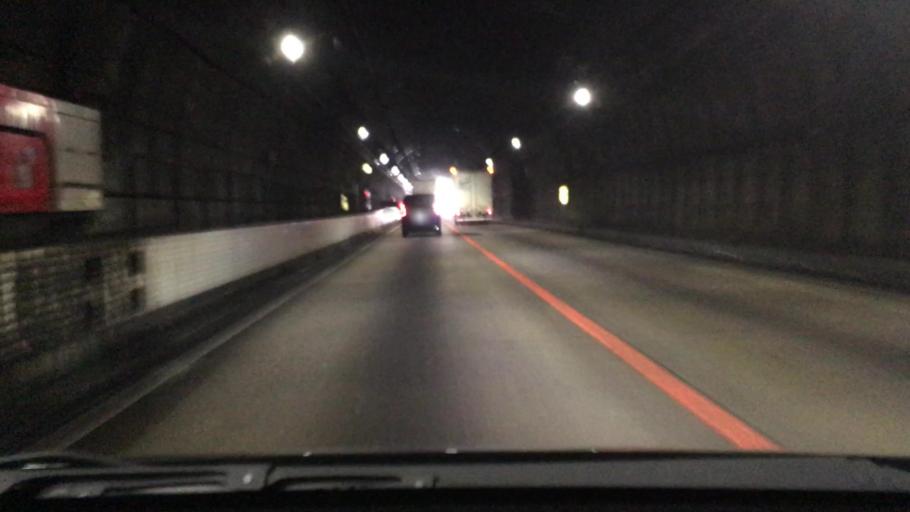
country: JP
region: Yamaguchi
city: Otake
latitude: 34.1836
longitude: 132.1707
